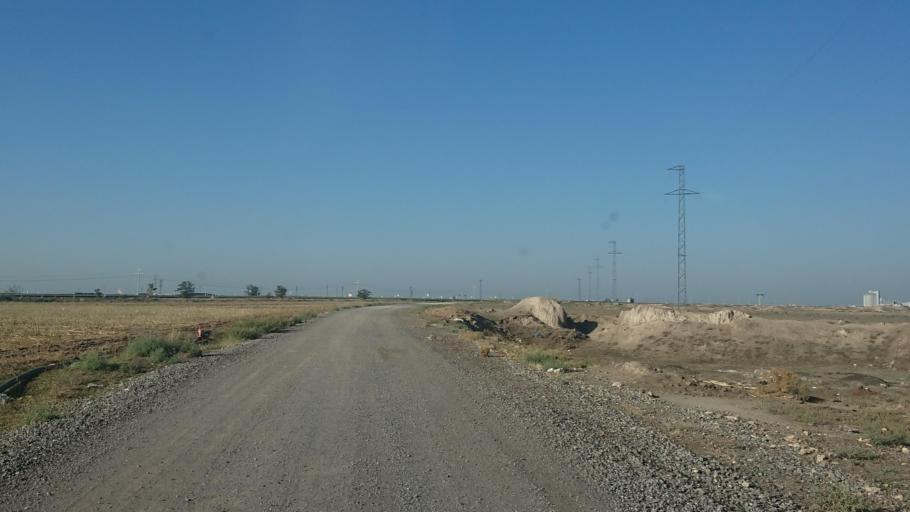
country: TR
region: Aksaray
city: Sultanhani
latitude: 38.2803
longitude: 33.7055
